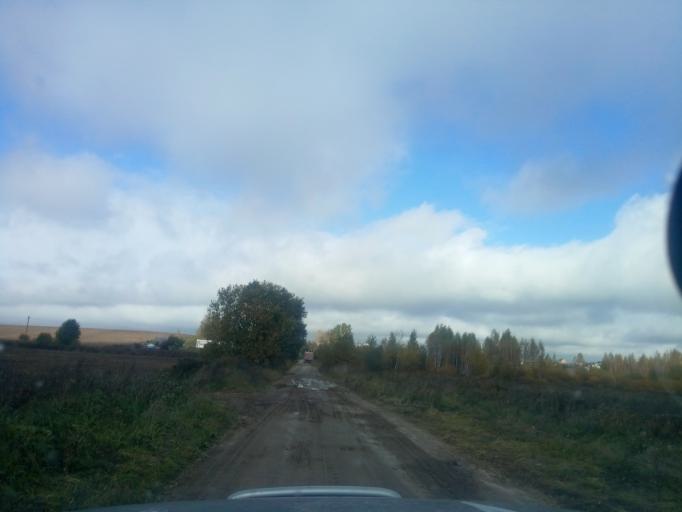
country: BY
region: Minsk
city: Zaslawye
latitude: 54.0219
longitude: 27.2884
